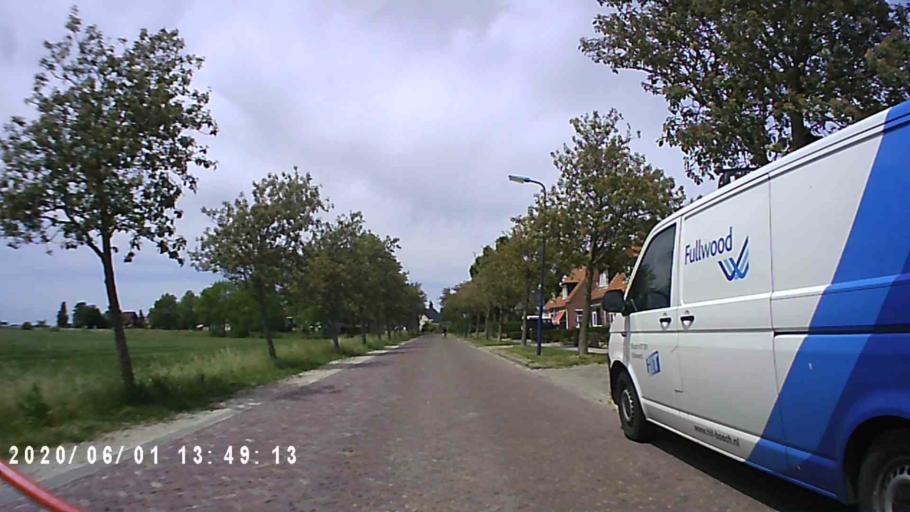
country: NL
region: Friesland
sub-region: Gemeente Littenseradiel
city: Wommels
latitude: 53.0947
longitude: 5.6179
